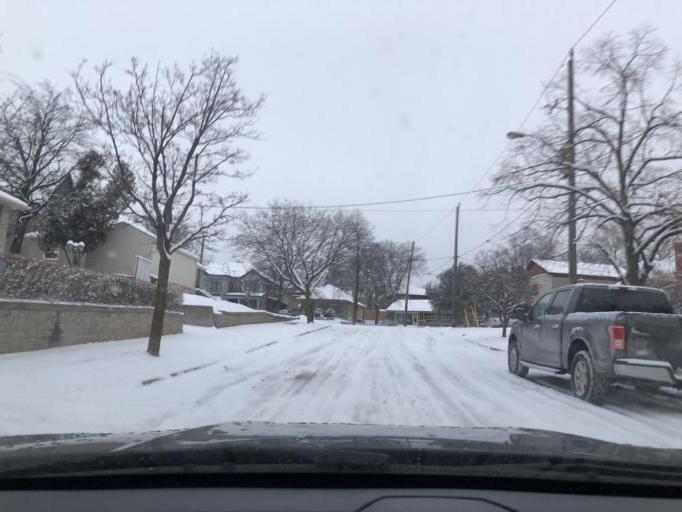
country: CA
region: Ontario
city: Toronto
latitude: 43.7011
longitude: -79.4833
